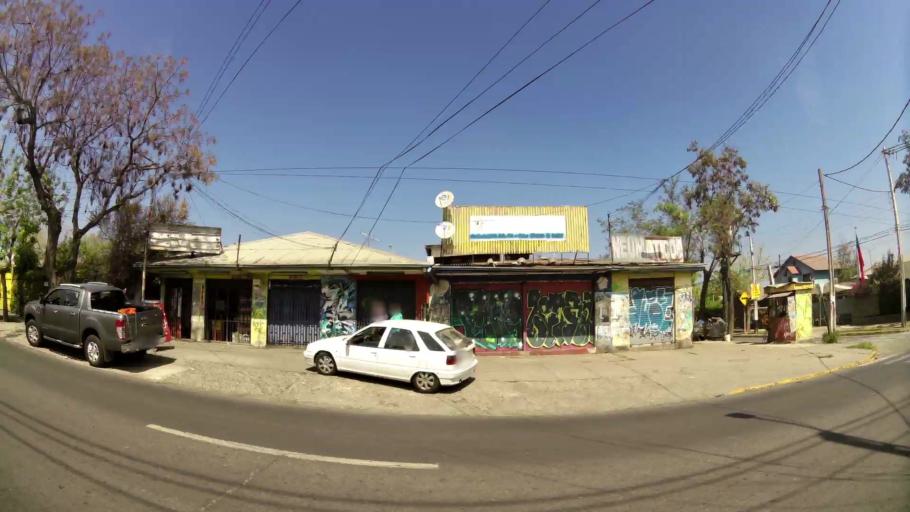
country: CL
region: Santiago Metropolitan
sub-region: Provincia de Santiago
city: Villa Presidente Frei, Nunoa, Santiago, Chile
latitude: -33.4709
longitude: -70.5459
